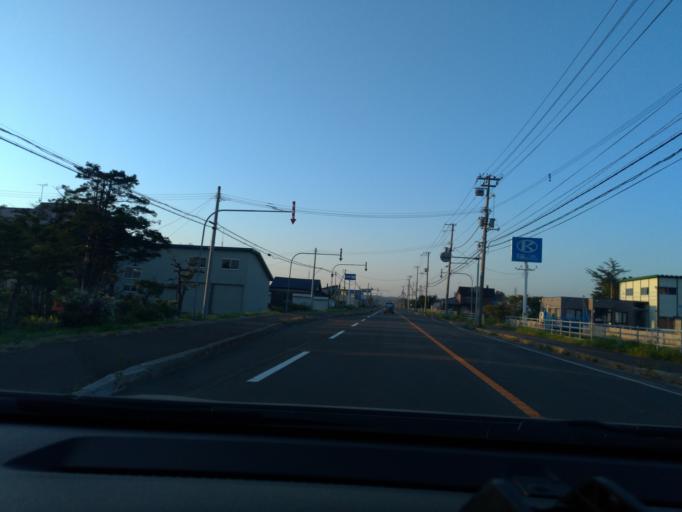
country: JP
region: Hokkaido
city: Tobetsu
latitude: 43.2023
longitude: 141.5212
